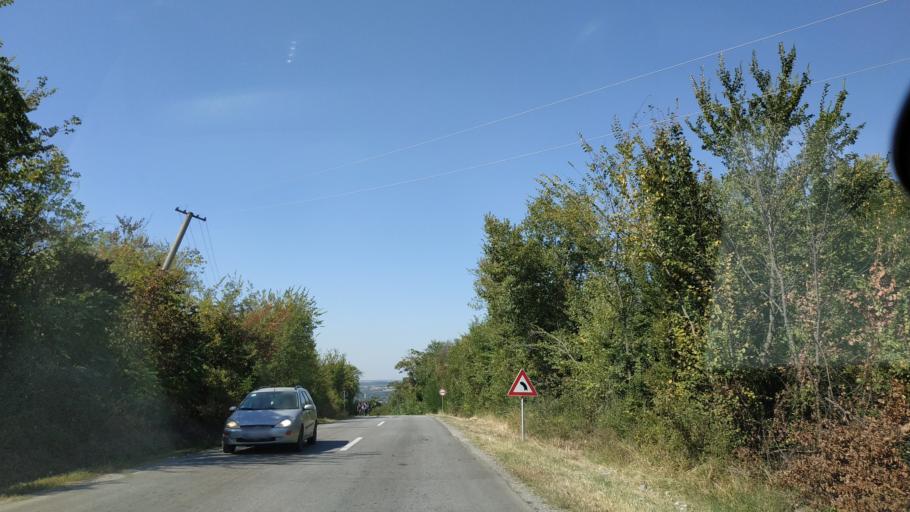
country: RS
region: Central Serbia
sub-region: Sumadijski Okrug
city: Raca
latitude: 44.2383
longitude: 20.8424
